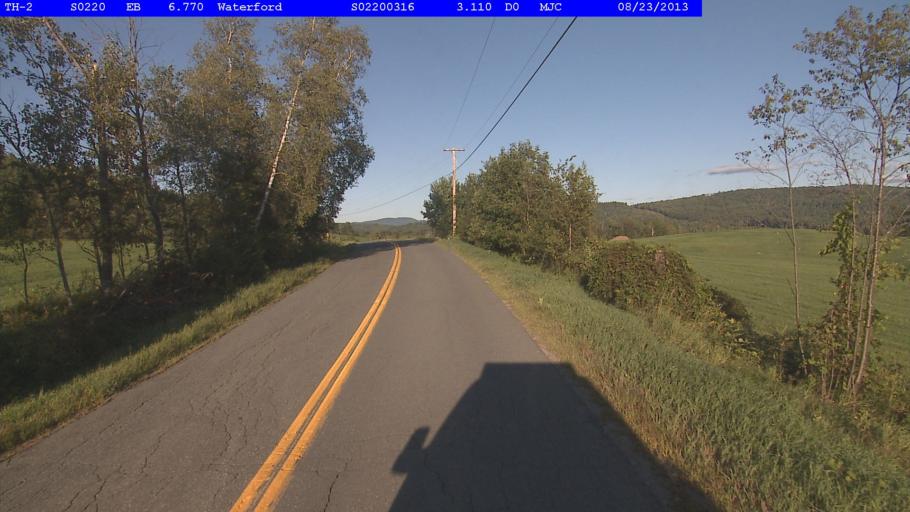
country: US
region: Vermont
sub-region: Caledonia County
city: Saint Johnsbury
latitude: 44.3394
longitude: -71.9415
